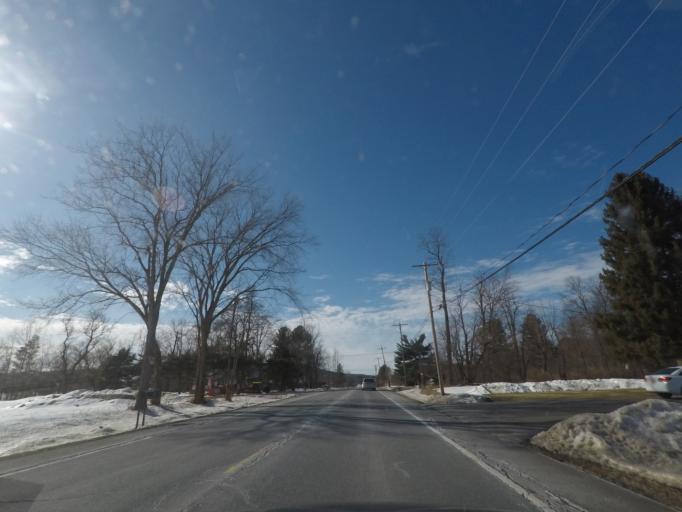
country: US
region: New York
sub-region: Albany County
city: Altamont
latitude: 42.7383
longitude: -74.0056
